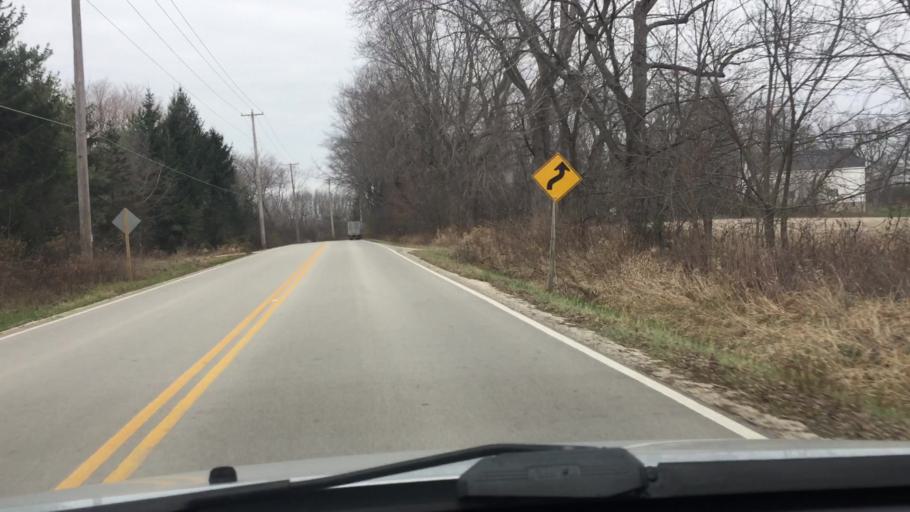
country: US
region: Wisconsin
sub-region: Ozaukee County
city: Cedarburg
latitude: 43.2726
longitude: -87.9730
